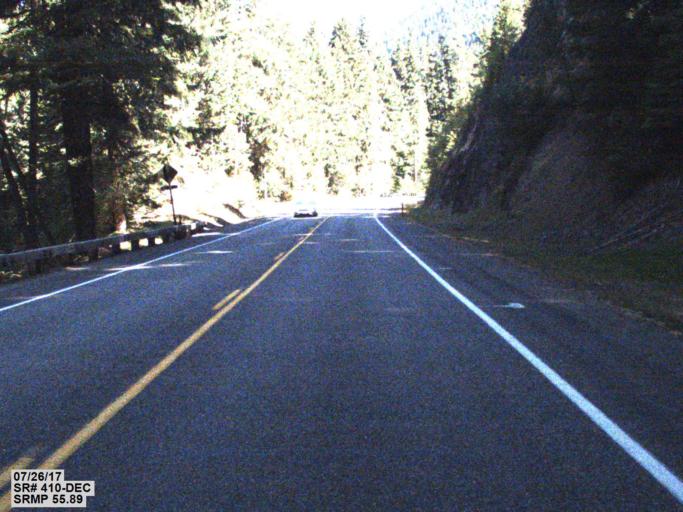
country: US
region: Washington
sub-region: King County
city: Enumclaw
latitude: 47.0026
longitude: -121.5287
